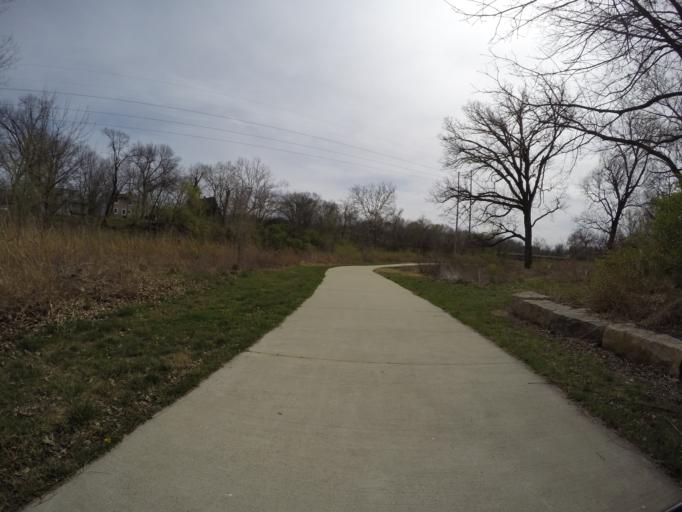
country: US
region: Kansas
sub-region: Johnson County
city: Leawood
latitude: 38.9499
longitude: -94.5787
